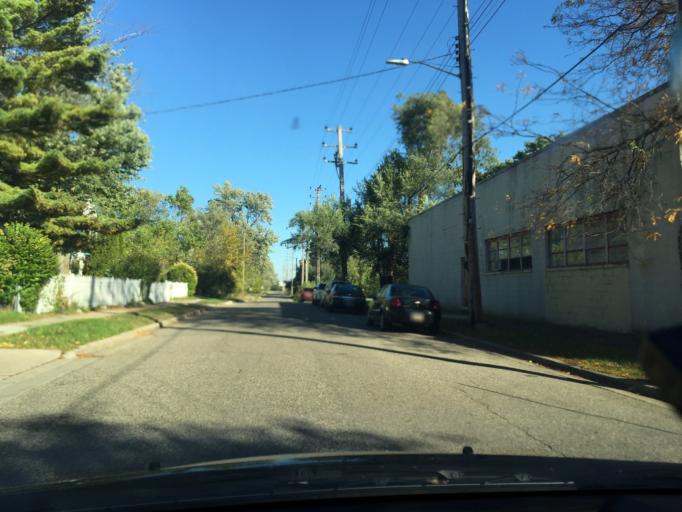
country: US
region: Michigan
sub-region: Oakland County
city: Pontiac
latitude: 42.6205
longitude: -83.2750
